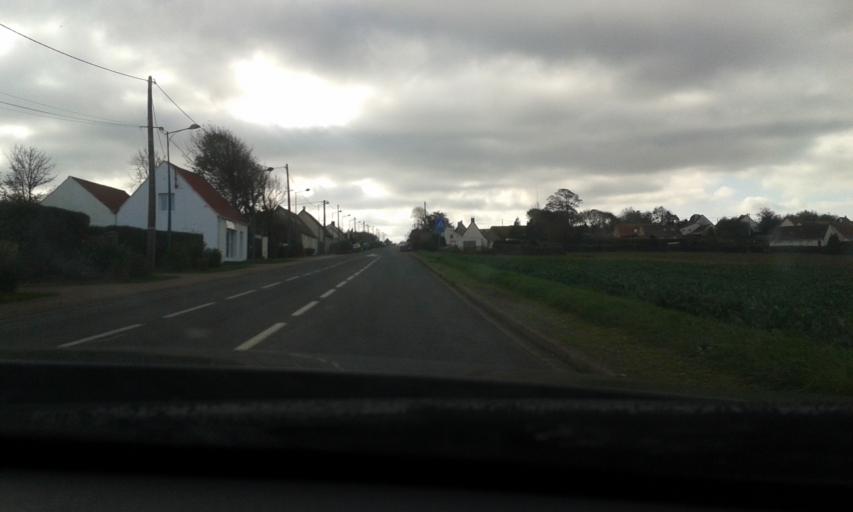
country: FR
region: Nord-Pas-de-Calais
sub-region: Departement du Pas-de-Calais
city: Ferques
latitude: 50.8711
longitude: 1.7423
